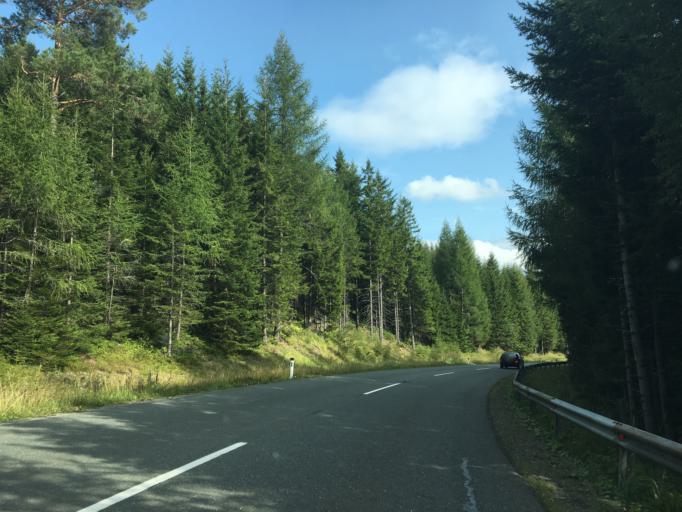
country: AT
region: Styria
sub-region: Politischer Bezirk Deutschlandsberg
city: Kloster
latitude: 46.8287
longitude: 15.0500
